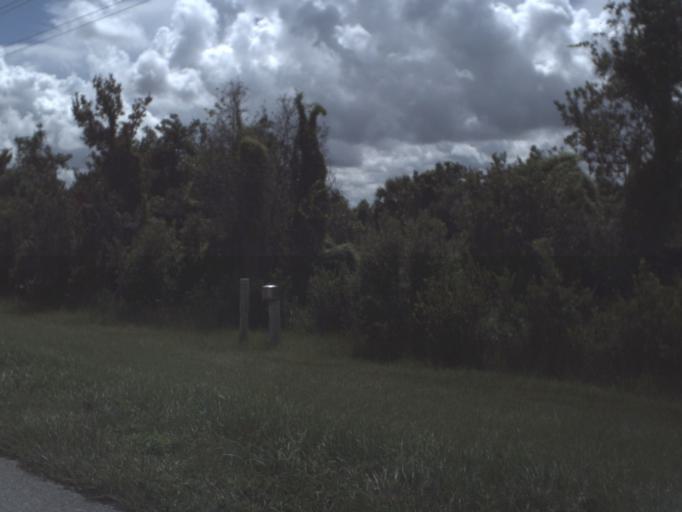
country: US
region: Florida
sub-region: Highlands County
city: Lake Placid
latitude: 27.4239
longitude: -81.2118
